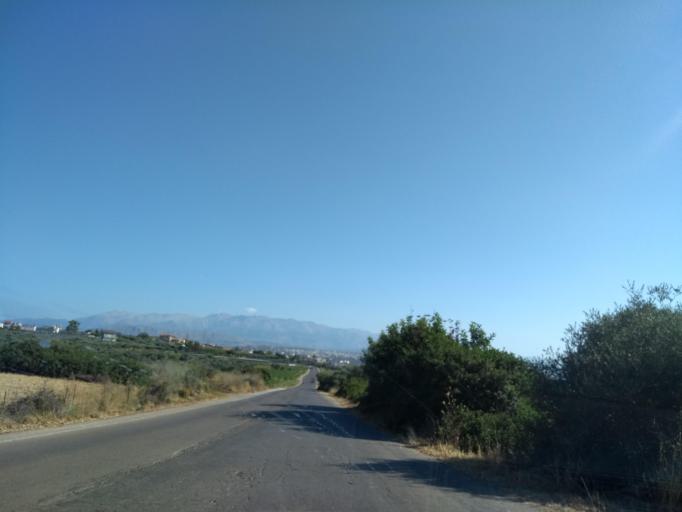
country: GR
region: Crete
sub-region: Nomos Chanias
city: Pithari
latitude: 35.5770
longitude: 24.0931
